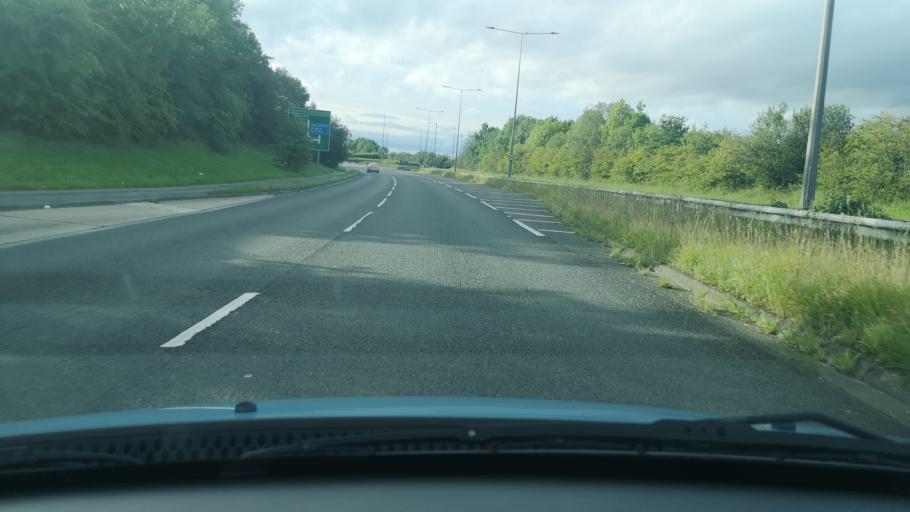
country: GB
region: England
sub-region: Doncaster
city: Carcroft
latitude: 53.5754
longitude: -1.2050
